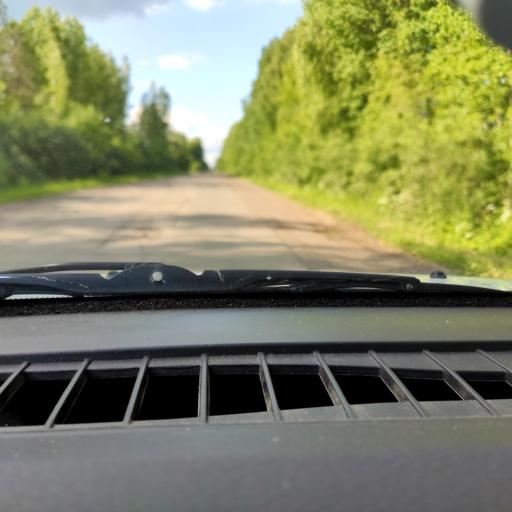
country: RU
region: Perm
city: Uinskoye
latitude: 57.2520
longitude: 56.5326
